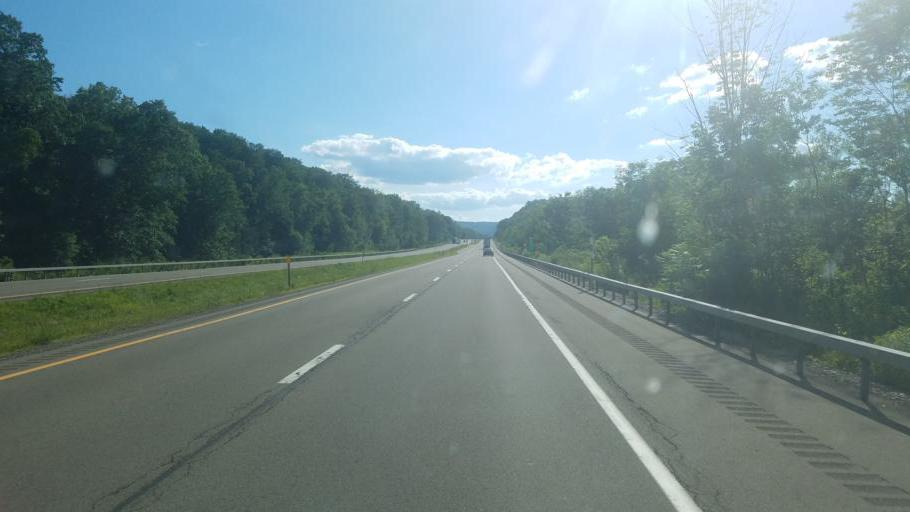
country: US
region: New York
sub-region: Cattaraugus County
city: Salamanca
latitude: 42.1024
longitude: -78.8331
